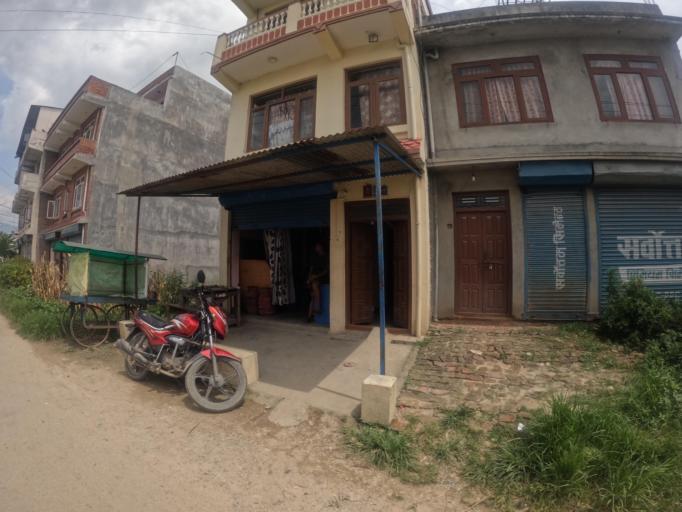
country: NP
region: Central Region
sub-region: Bagmati Zone
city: Bhaktapur
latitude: 27.6877
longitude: 85.3827
